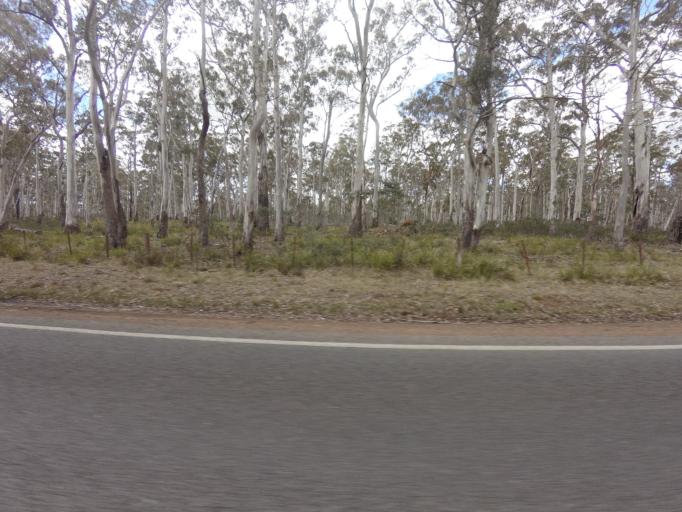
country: AU
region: Tasmania
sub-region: Northern Midlands
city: Evandale
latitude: -41.9721
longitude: 147.6484
